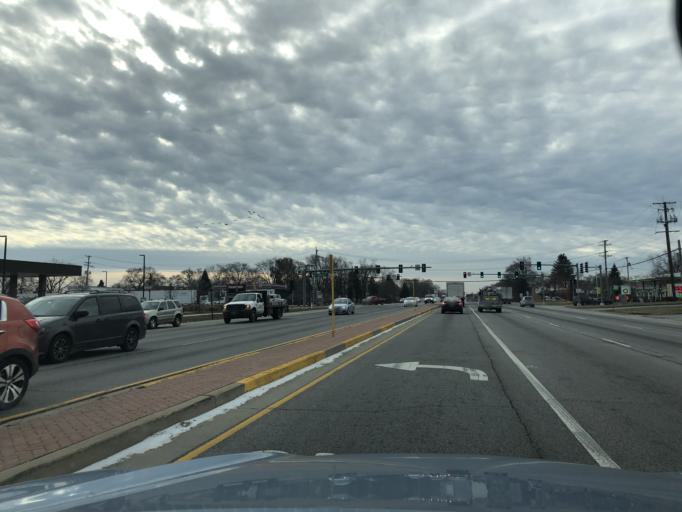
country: US
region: Illinois
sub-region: DuPage County
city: Wood Dale
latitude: 41.9728
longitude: -87.9593
